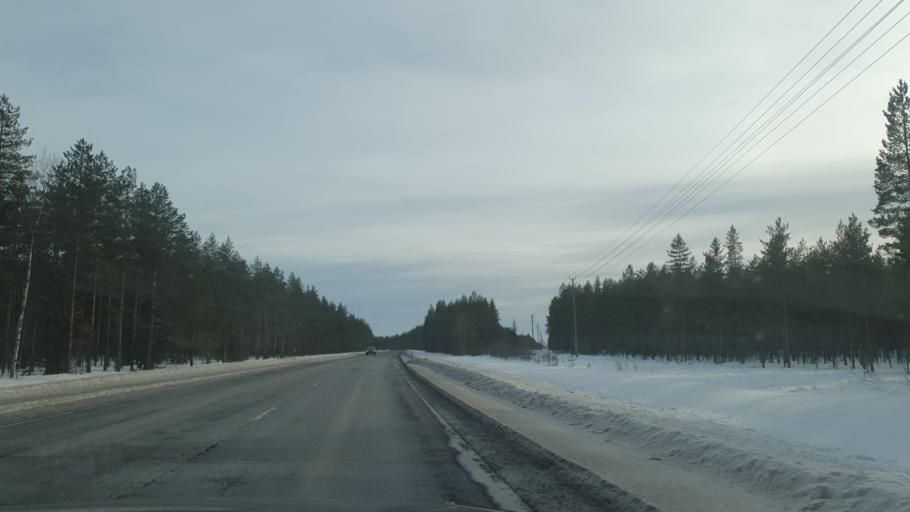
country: FI
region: Northern Ostrobothnia
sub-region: Oulunkaari
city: Utajaervi
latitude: 64.6567
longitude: 26.5577
